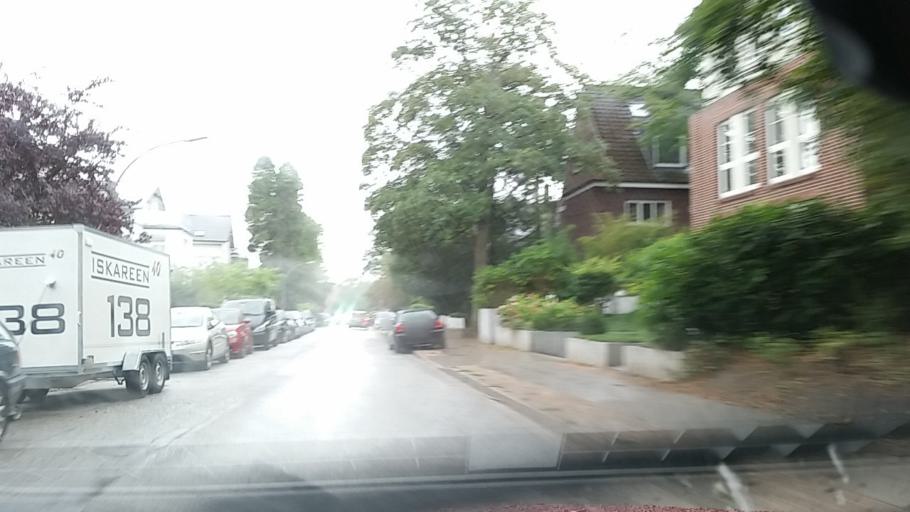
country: DE
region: Schleswig-Holstein
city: Halstenbek
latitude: 53.5616
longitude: 9.8083
